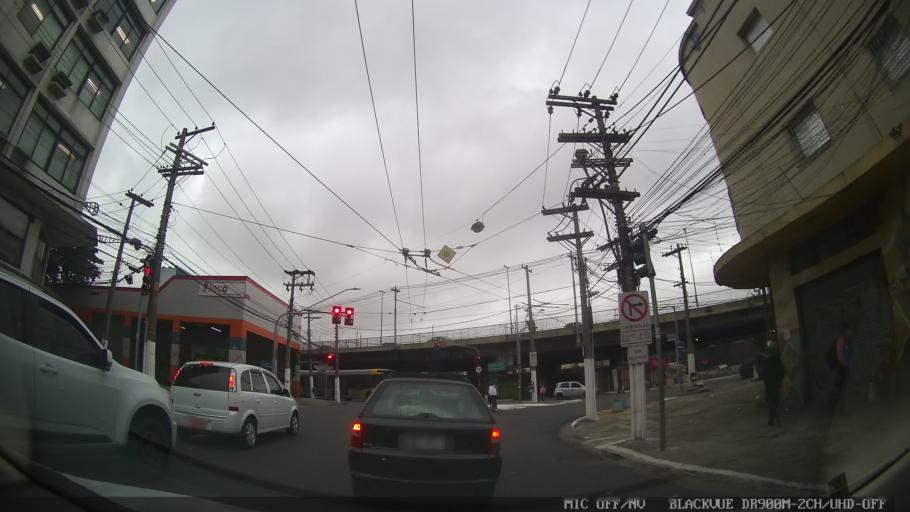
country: BR
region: Sao Paulo
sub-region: Sao Caetano Do Sul
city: Sao Caetano do Sul
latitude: -23.5538
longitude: -46.5548
